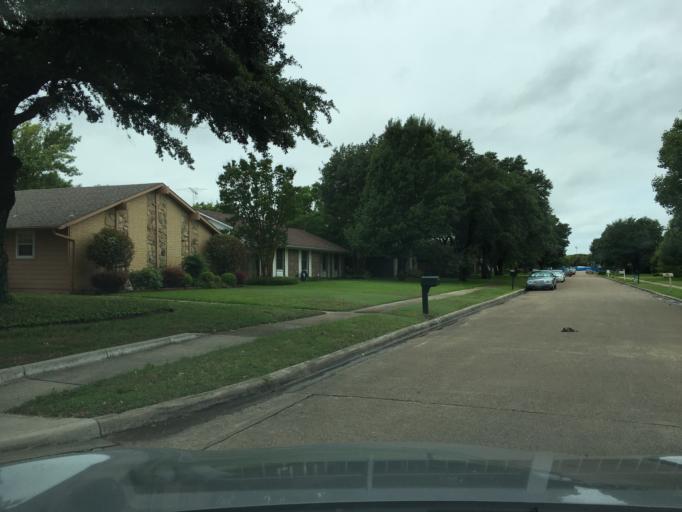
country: US
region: Texas
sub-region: Dallas County
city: Richardson
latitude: 32.9353
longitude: -96.6874
